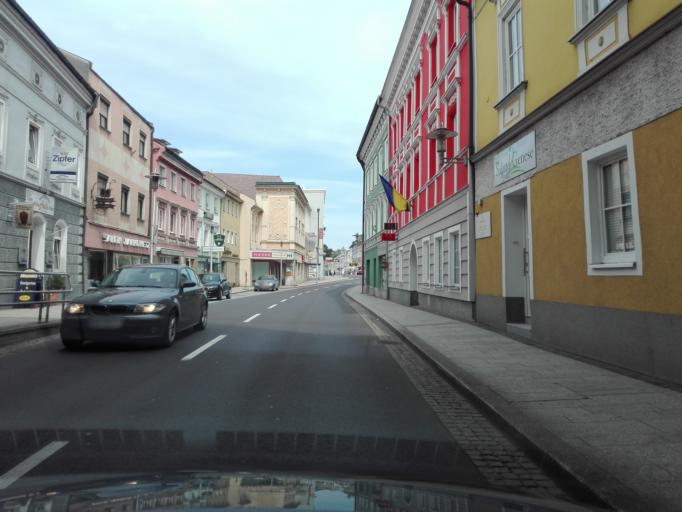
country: AT
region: Upper Austria
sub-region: Politischer Bezirk Vocklabruck
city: Schwanenstadt
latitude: 48.0543
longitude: 13.7726
